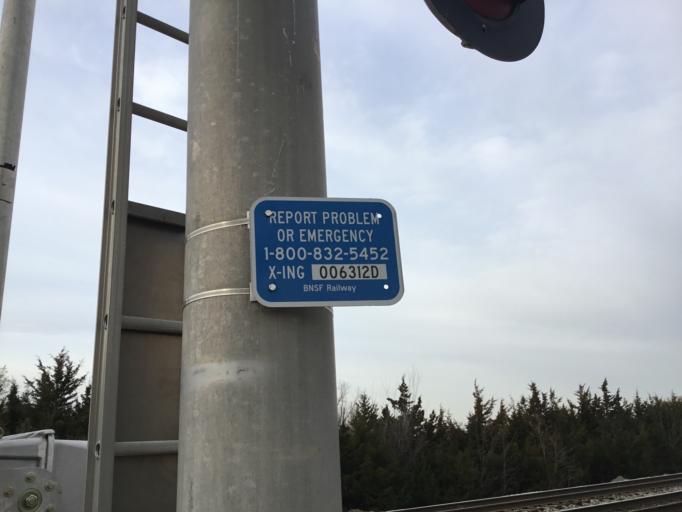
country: US
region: Kansas
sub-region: Lyon County
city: Emporia
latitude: 38.4009
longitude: -96.1618
